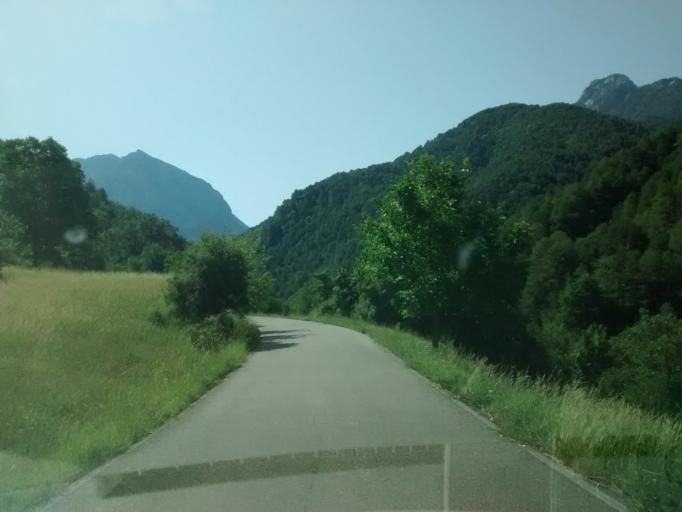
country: ES
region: Aragon
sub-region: Provincia de Huesca
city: Laspuna
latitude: 42.5405
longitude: 0.1947
